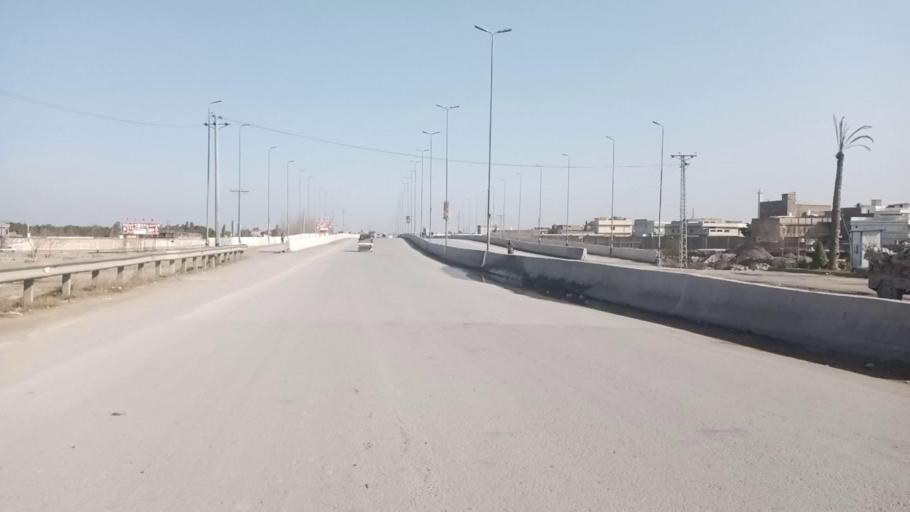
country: PK
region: Khyber Pakhtunkhwa
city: Peshawar
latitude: 34.0343
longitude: 71.5644
